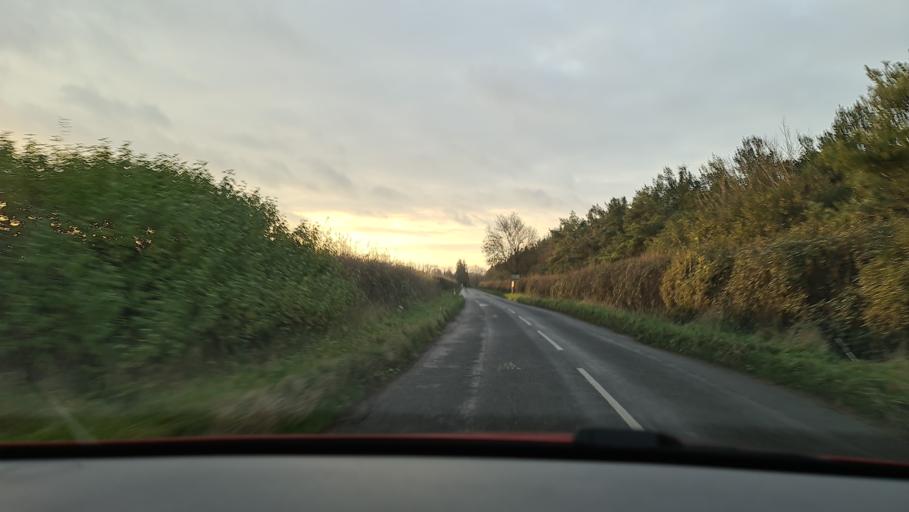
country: GB
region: England
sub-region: Oxfordshire
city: Kidlington
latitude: 51.8839
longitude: -1.2745
